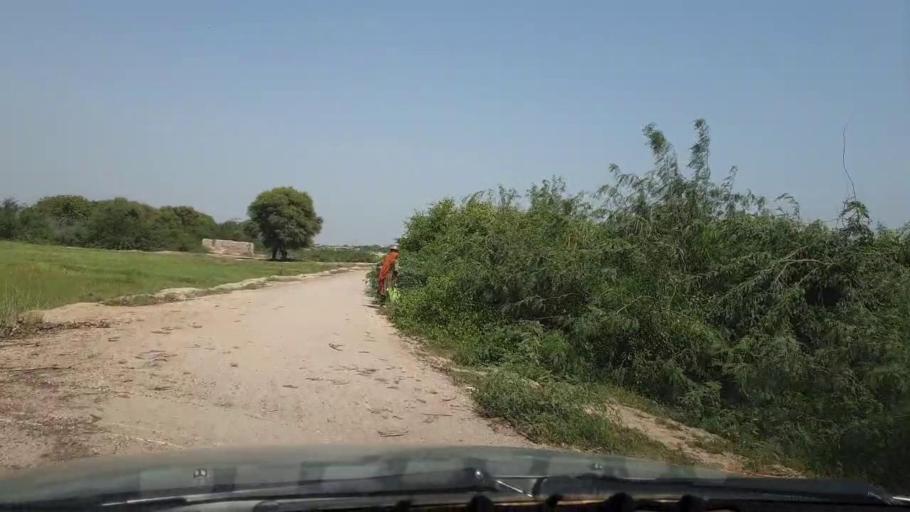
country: PK
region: Sindh
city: Chambar
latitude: 25.1957
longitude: 68.7136
